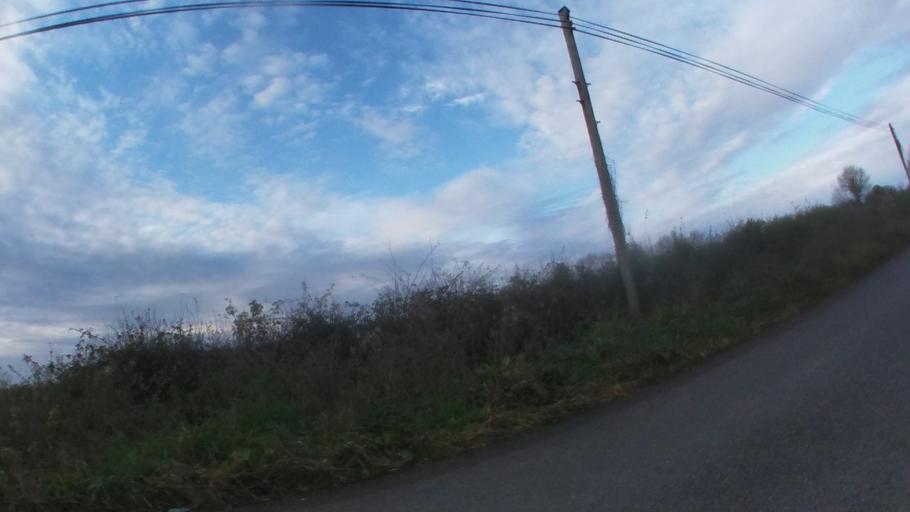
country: IE
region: Leinster
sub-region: Kilkenny
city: Kilkenny
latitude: 52.6864
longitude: -7.1755
